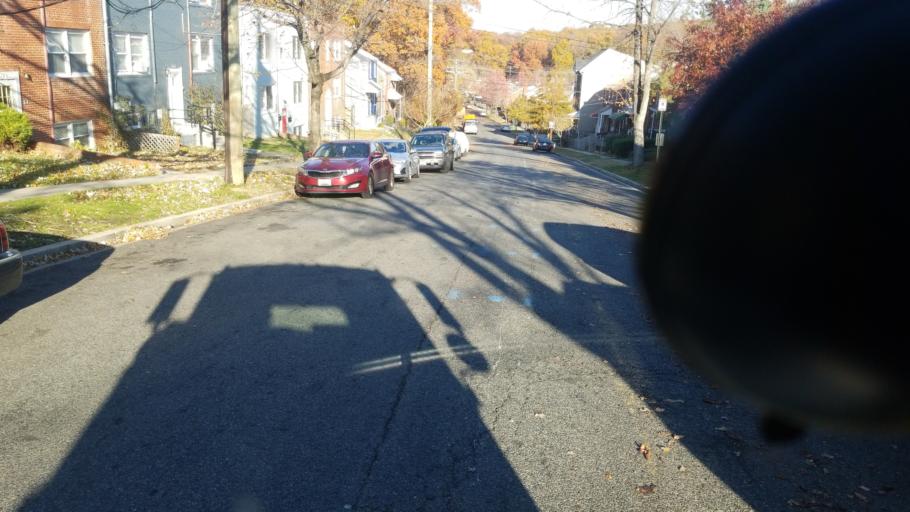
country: US
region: Maryland
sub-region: Prince George's County
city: Coral Hills
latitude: 38.8838
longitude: -76.9431
